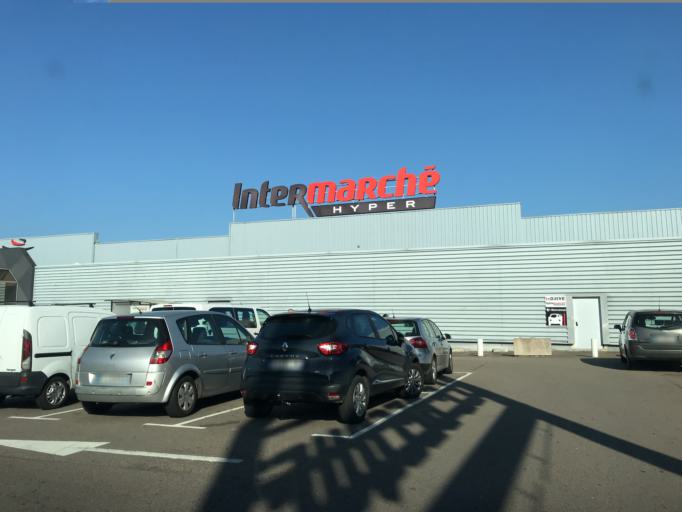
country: FR
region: Haute-Normandie
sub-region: Departement de l'Eure
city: Louviers
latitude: 49.2104
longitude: 1.1827
